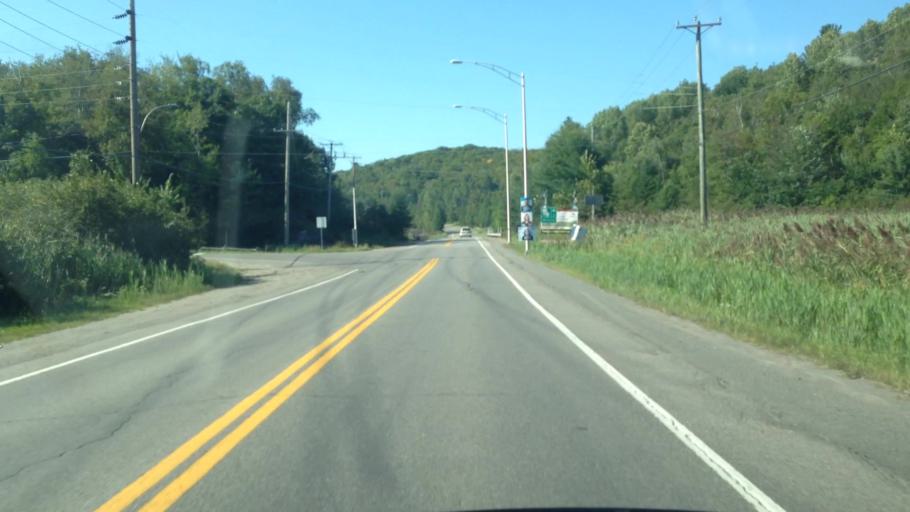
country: CA
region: Quebec
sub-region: Laurentides
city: Prevost
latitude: 45.9072
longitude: -74.0052
